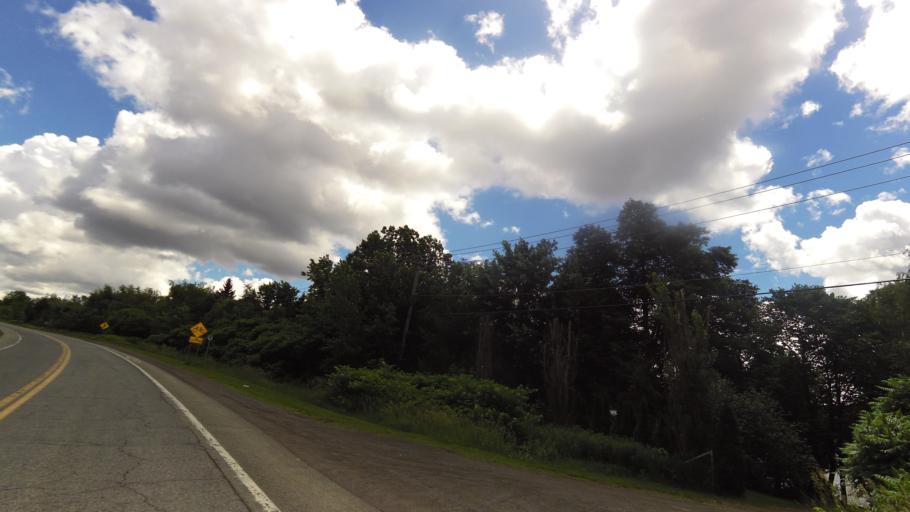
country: CA
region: Quebec
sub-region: Monteregie
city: Rigaud
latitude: 45.5280
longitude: -74.2783
